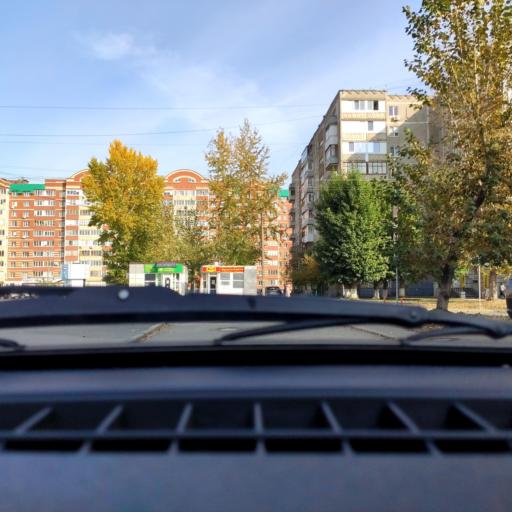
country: RU
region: Bashkortostan
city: Ufa
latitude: 54.7667
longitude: 56.0611
